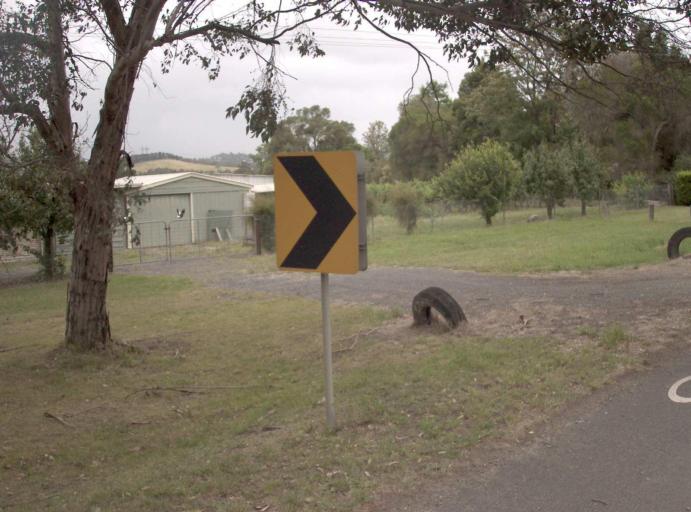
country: AU
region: Victoria
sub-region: Yarra Ranges
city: Lilydale
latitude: -37.7199
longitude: 145.3839
